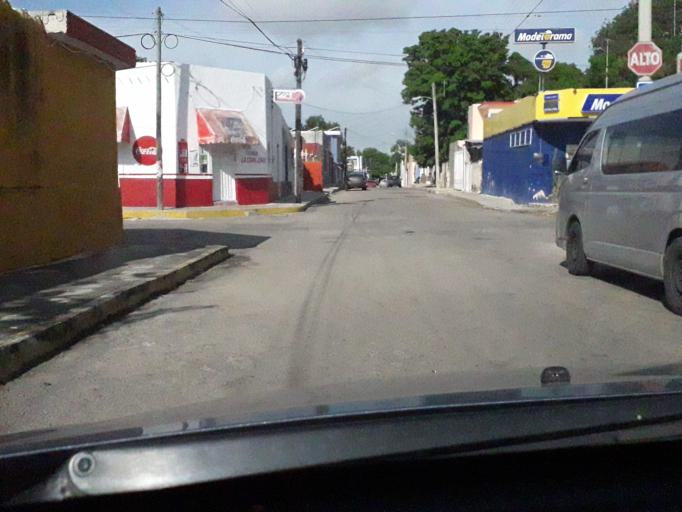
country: MX
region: Yucatan
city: Merida
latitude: 20.9561
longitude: -89.6175
